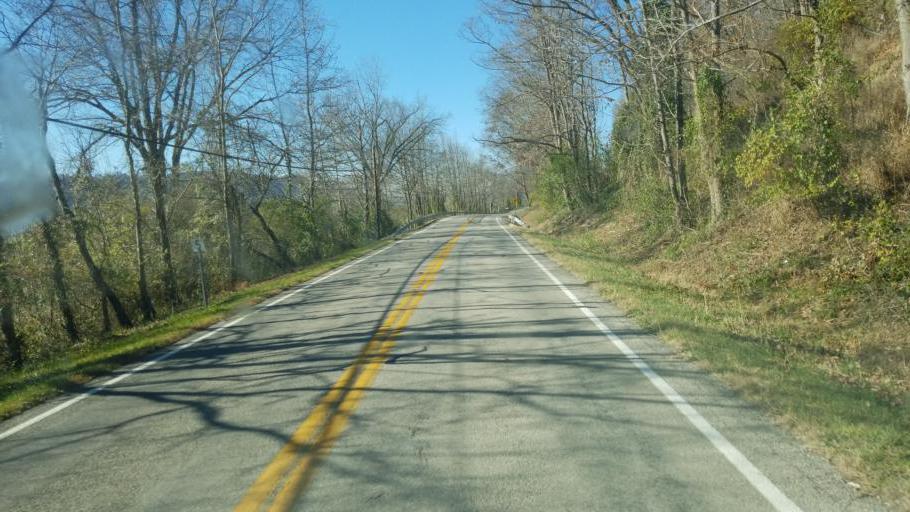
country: US
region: Kentucky
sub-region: Lewis County
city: Vanceburg
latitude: 38.6225
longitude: -83.1892
